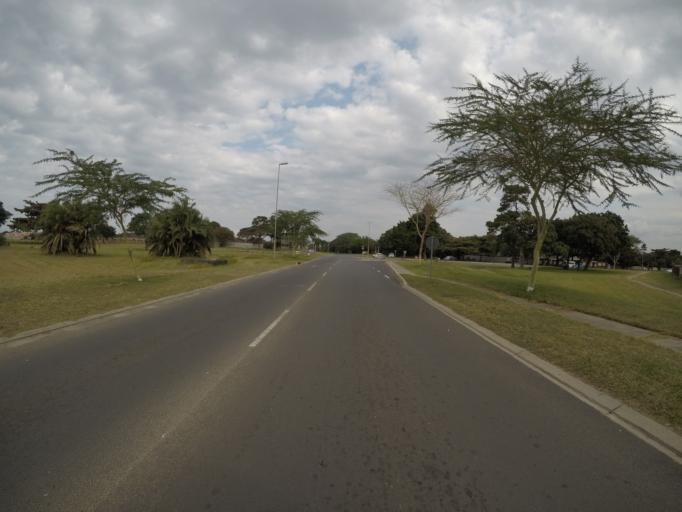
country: ZA
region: KwaZulu-Natal
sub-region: uThungulu District Municipality
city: Richards Bay
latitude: -28.7395
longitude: 32.0777
